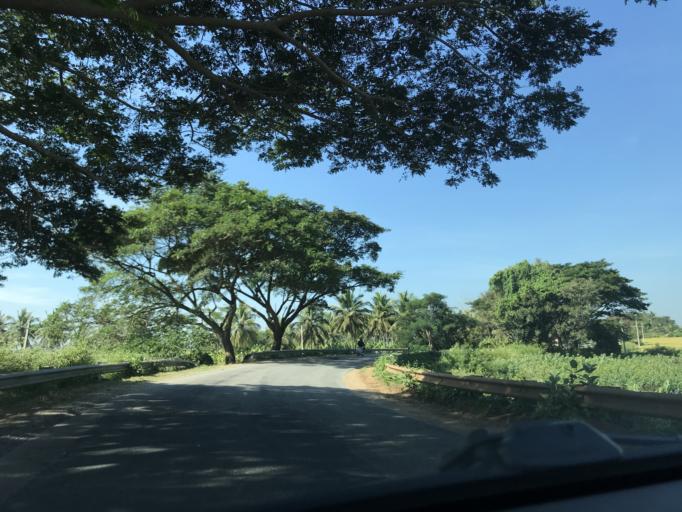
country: IN
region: Karnataka
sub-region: Mysore
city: Heggadadevankote
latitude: 12.1248
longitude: 76.4288
